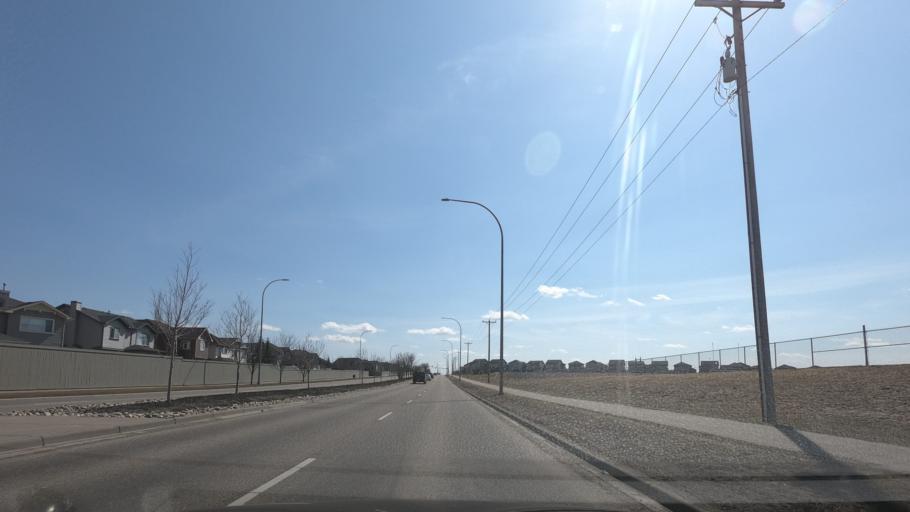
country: CA
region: Alberta
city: Airdrie
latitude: 51.2699
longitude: -114.0252
